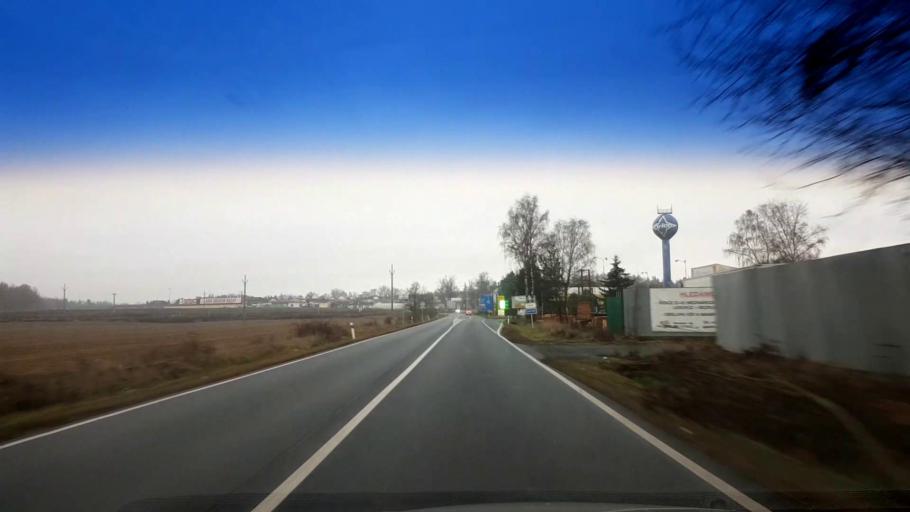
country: CZ
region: Karlovarsky
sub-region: Okres Cheb
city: Cheb
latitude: 50.0527
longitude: 12.3556
